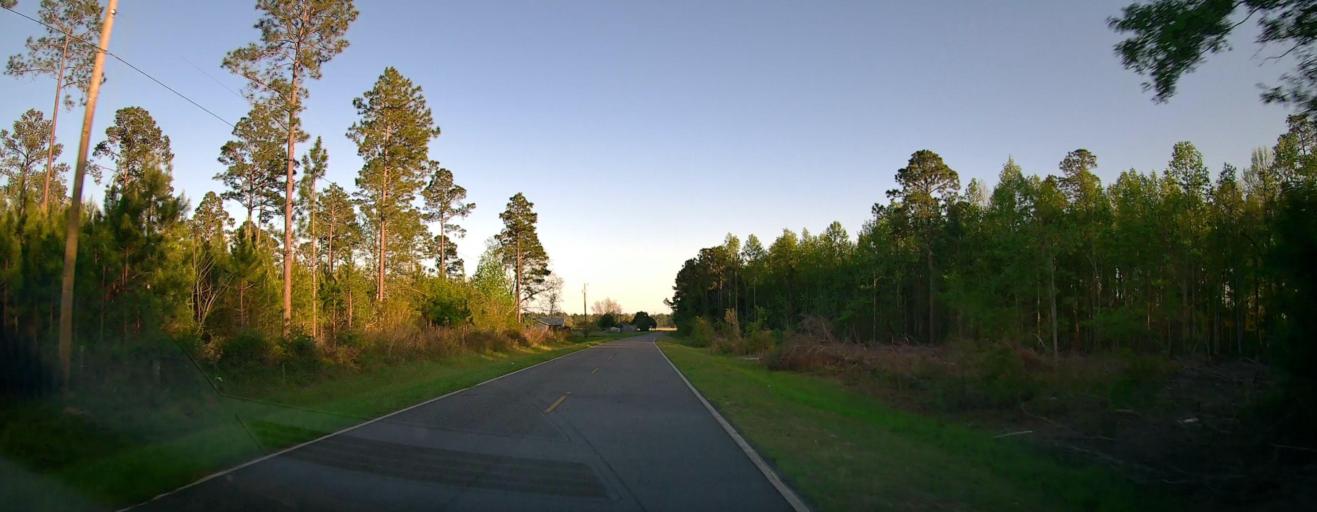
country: US
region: Georgia
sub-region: Ben Hill County
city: Fitzgerald
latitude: 31.6734
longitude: -83.2145
